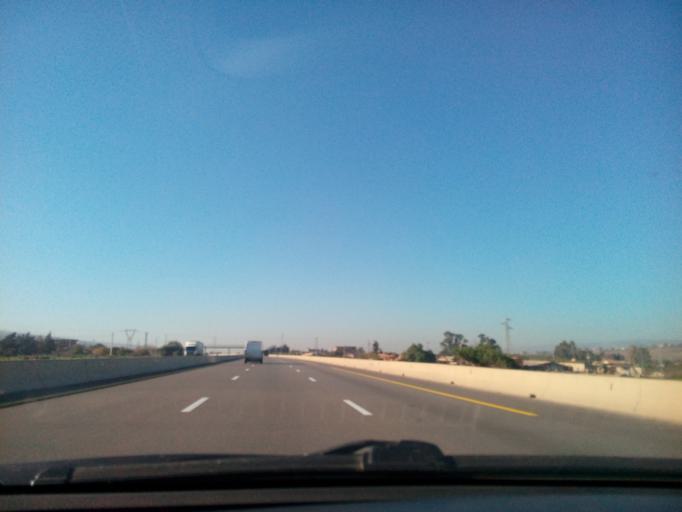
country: DZ
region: Chlef
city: Boukadir
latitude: 36.0325
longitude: 1.0730
